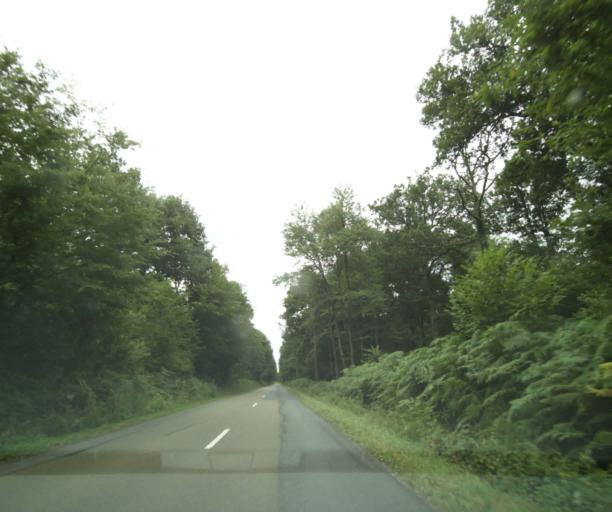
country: FR
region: Pays de la Loire
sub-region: Departement de la Sarthe
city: Precigne
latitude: 47.7418
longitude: -0.2810
